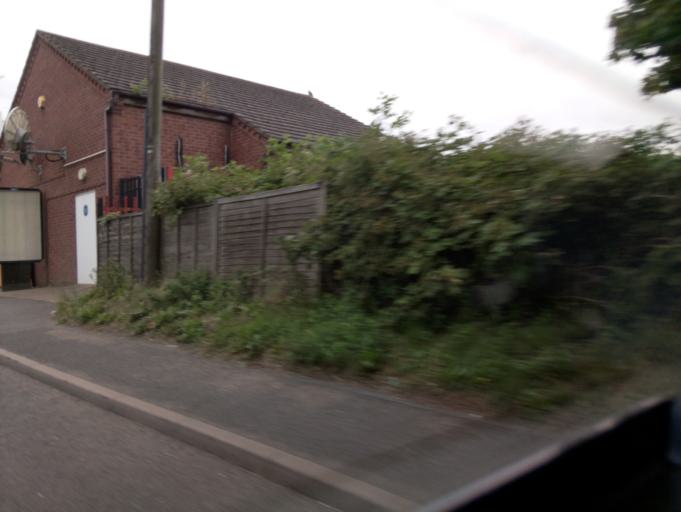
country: GB
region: England
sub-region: Worcestershire
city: Droitwich
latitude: 52.2937
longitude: -2.1132
